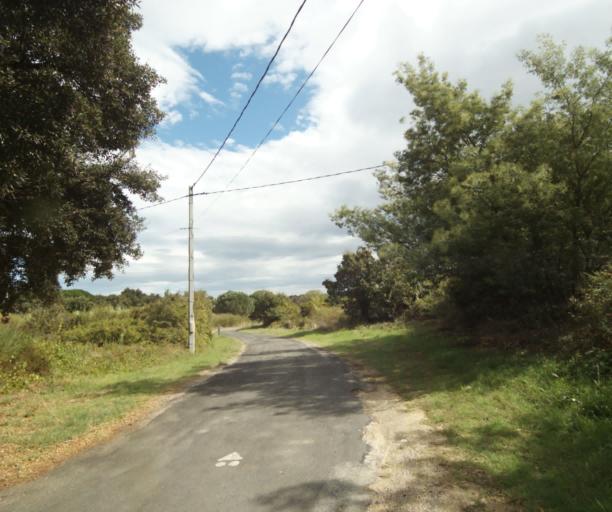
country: FR
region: Languedoc-Roussillon
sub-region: Departement des Pyrenees-Orientales
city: Argelers
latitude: 42.5354
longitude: 3.0422
